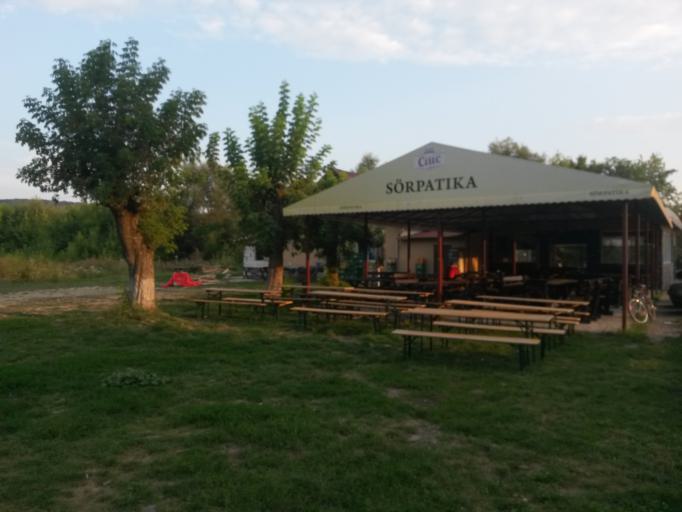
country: RO
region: Mures
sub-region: Comuna Santana de Mures
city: Santana de Mures
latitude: 46.5639
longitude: 24.5703
